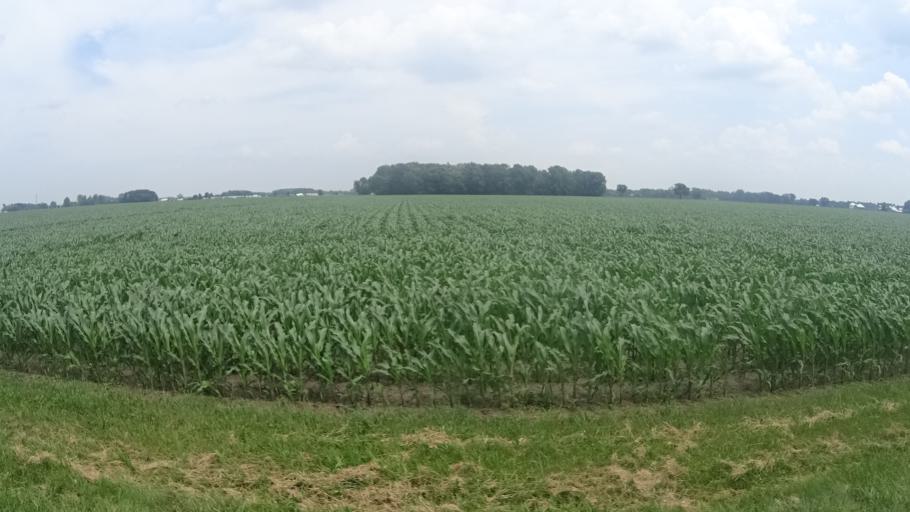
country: US
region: Ohio
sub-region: Erie County
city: Milan
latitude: 41.3128
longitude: -82.6328
